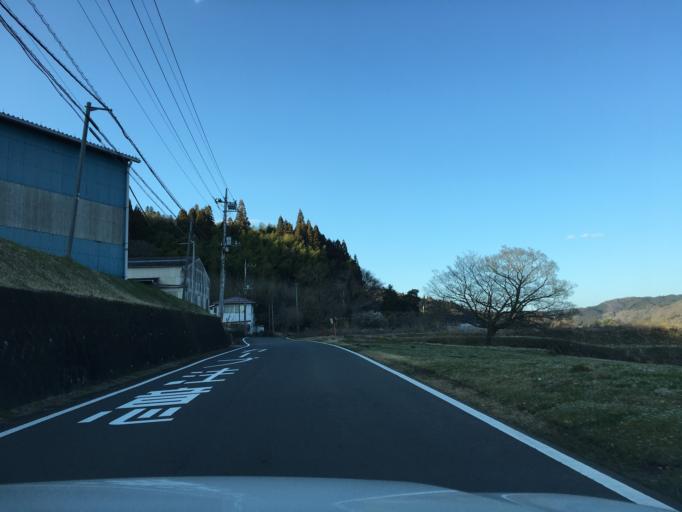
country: JP
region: Tochigi
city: Karasuyama
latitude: 36.7709
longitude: 140.2059
